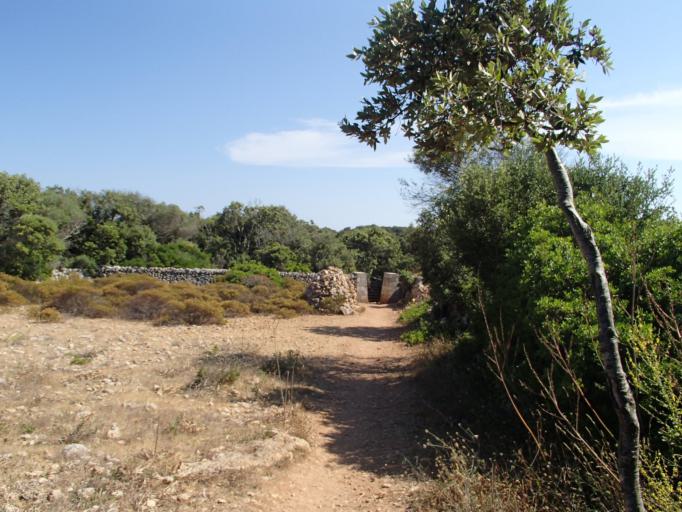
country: ES
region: Balearic Islands
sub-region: Illes Balears
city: Es Castell
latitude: 39.8427
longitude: 4.2943
